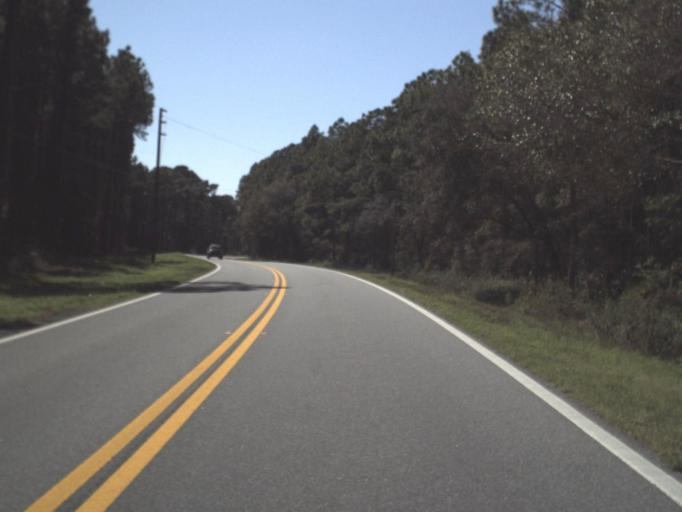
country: US
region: Florida
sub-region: Franklin County
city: Carrabelle
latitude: 29.9130
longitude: -84.5307
